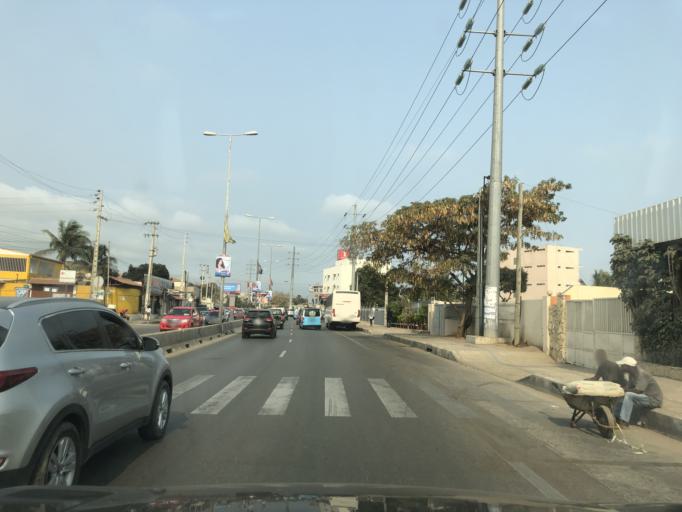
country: AO
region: Luanda
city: Luanda
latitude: -8.8935
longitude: 13.1840
